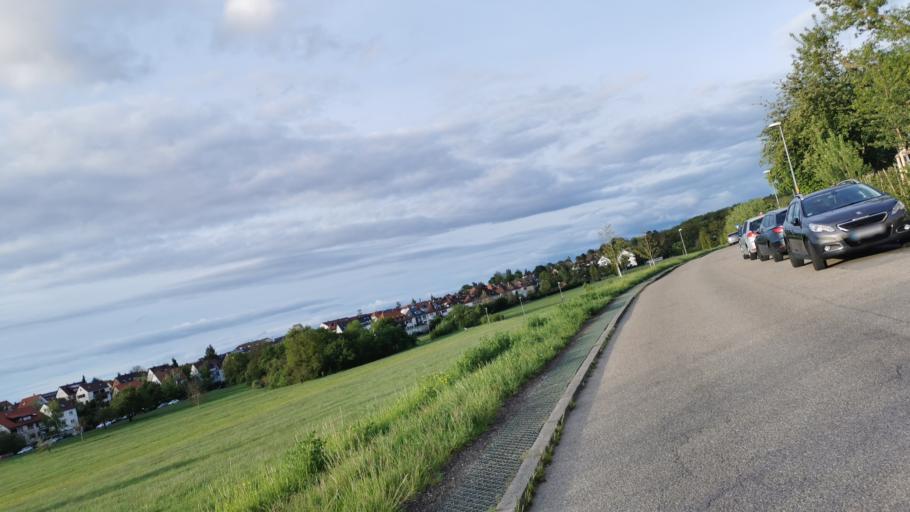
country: DE
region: Baden-Wuerttemberg
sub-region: Regierungsbezirk Stuttgart
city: Korntal
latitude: 48.8201
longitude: 9.1140
